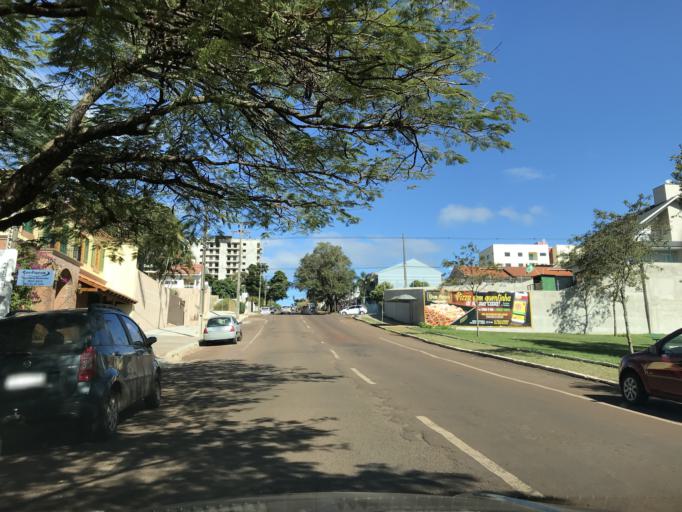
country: BR
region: Parana
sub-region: Cascavel
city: Cascavel
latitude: -24.9483
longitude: -53.4689
